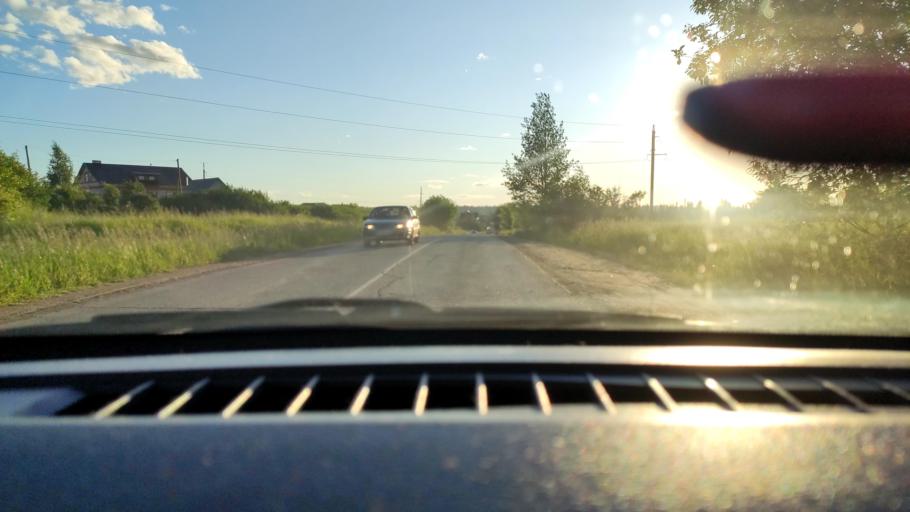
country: RU
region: Perm
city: Kultayevo
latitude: 57.9286
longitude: 55.8681
